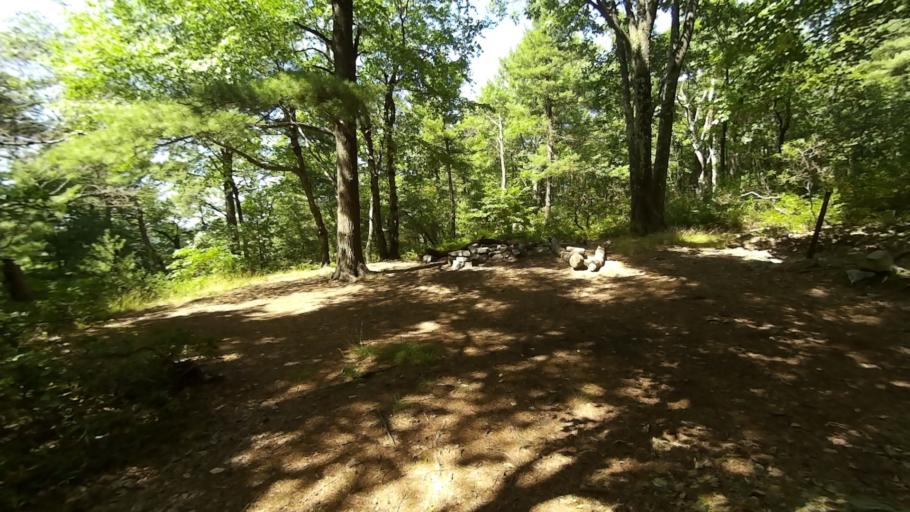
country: US
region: Pennsylvania
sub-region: Centre County
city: Boalsburg
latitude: 40.7299
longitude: -77.7845
